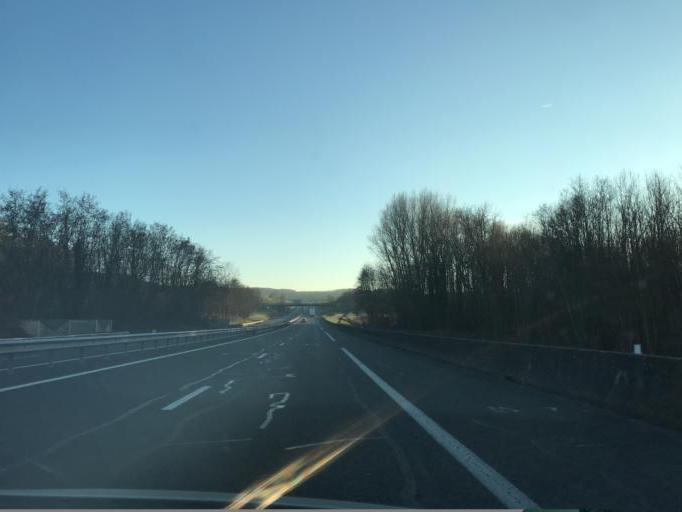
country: FR
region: Bourgogne
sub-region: Departement de l'Yonne
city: Saint-Martin-du-Tertre
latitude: 48.2260
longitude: 3.2406
